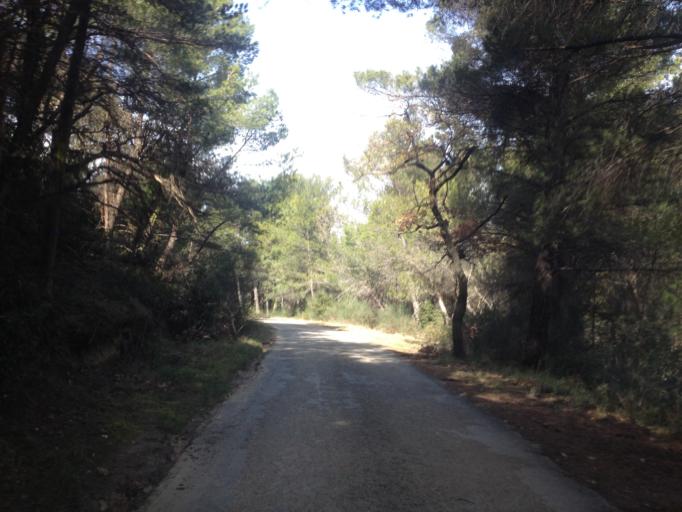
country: FR
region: Provence-Alpes-Cote d'Azur
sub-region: Departement du Vaucluse
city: Sablet
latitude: 44.1827
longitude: 5.0128
